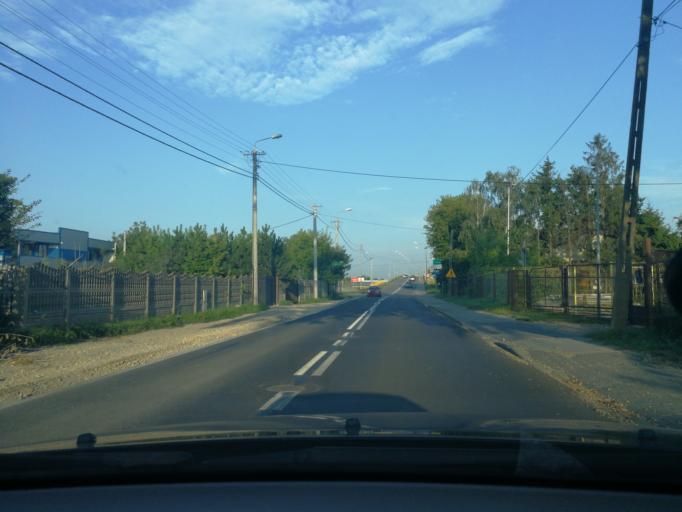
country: PL
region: Masovian Voivodeship
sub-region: Powiat warszawski zachodni
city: Ozarow Mazowiecki
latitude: 52.1859
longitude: 20.7692
